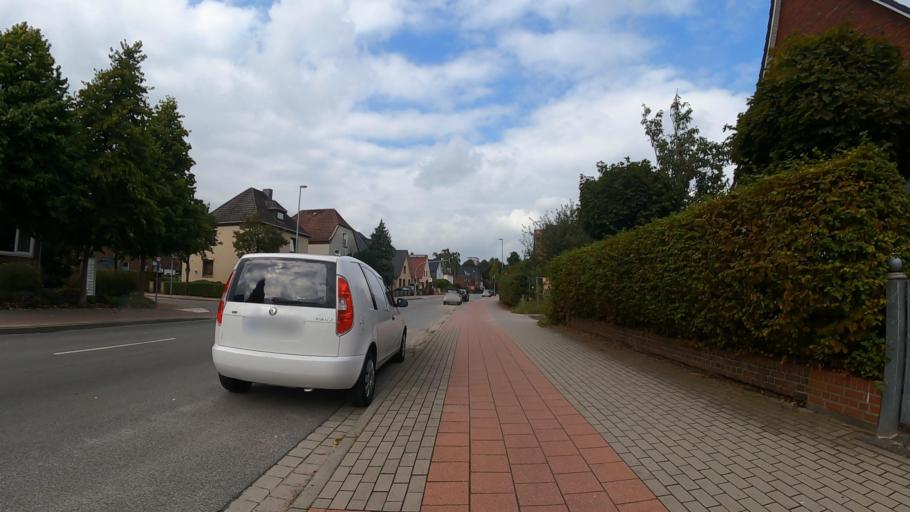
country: DE
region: Schleswig-Holstein
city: Elmshorn
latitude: 53.7449
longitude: 9.6598
